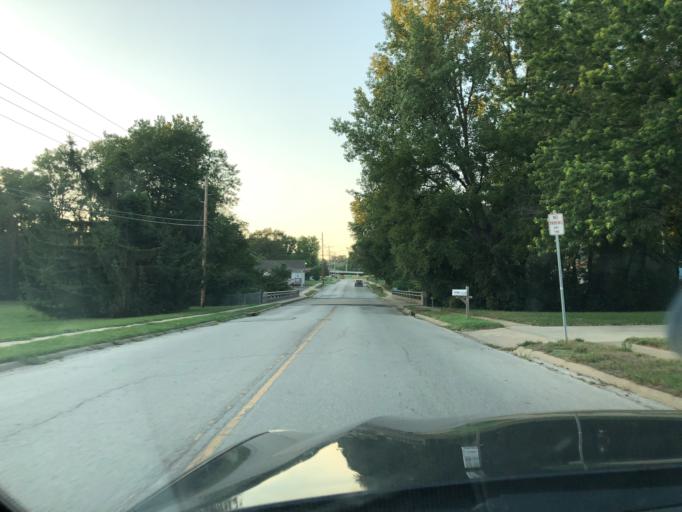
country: US
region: Kansas
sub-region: Leavenworth County
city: Leavenworth
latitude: 39.3239
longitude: -94.9506
